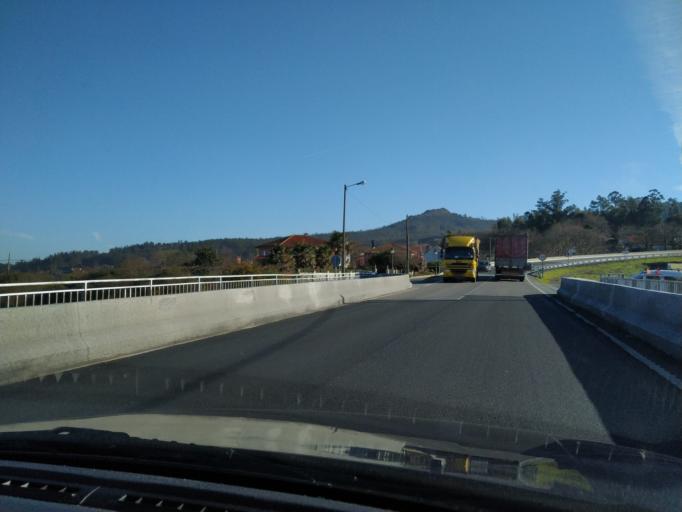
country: ES
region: Galicia
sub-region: Provincia da Coruna
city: Vedra
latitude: 42.7996
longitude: -8.4749
